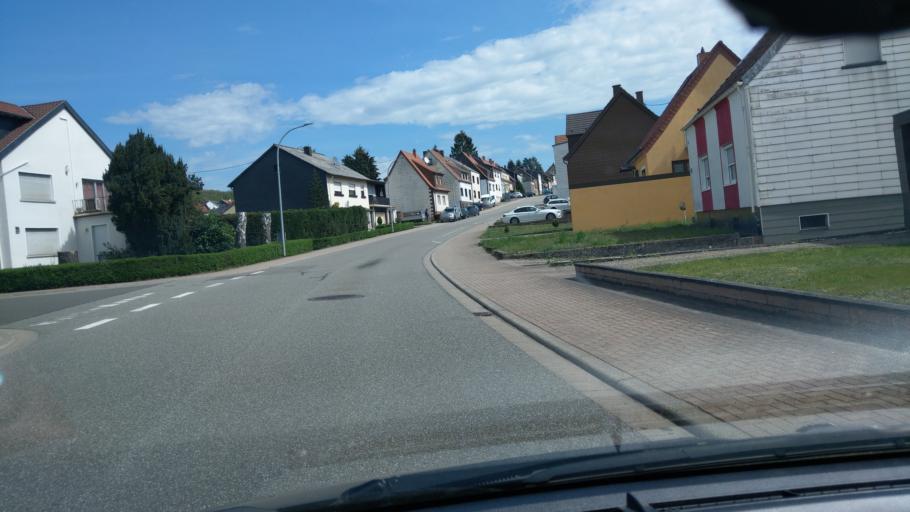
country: DE
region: Saarland
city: Spiesen-Elversberg
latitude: 49.3064
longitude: 7.1378
